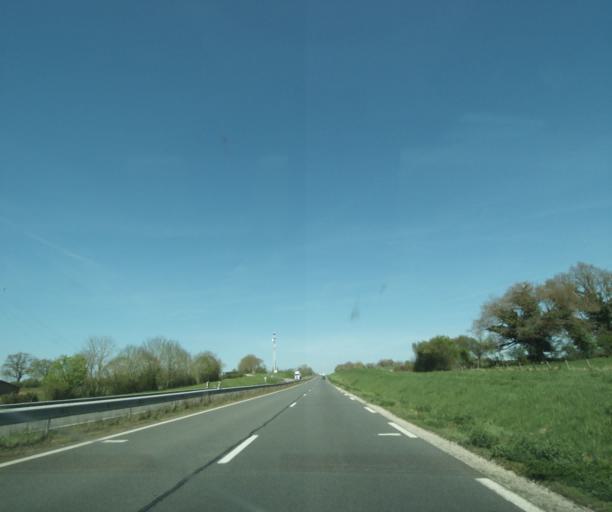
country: FR
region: Bourgogne
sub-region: Departement de la Nievre
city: Saint-Pierre-le-Moutier
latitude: 46.7771
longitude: 3.1308
